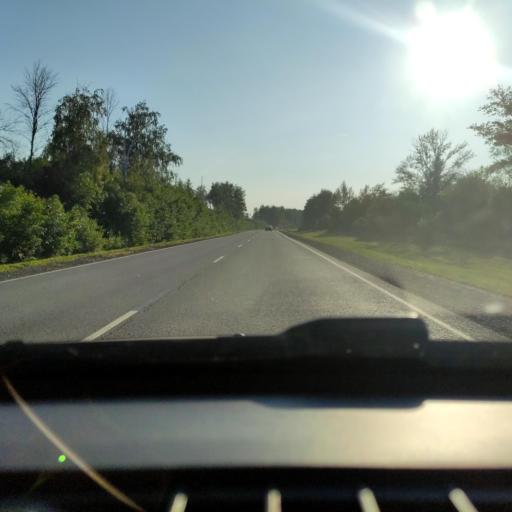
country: RU
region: Voronezj
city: Kashirskoye
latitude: 51.4586
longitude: 39.7742
